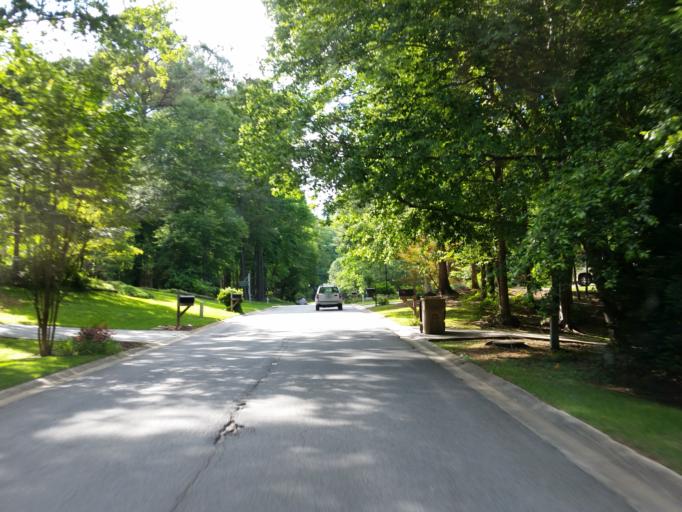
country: US
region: Georgia
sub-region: Fulton County
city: Roswell
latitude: 34.0071
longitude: -84.4193
